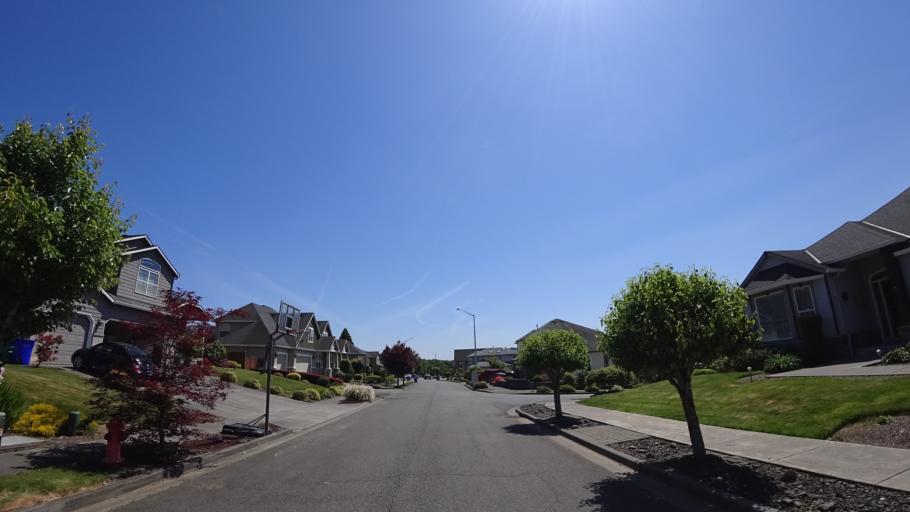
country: US
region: Oregon
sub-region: Clackamas County
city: Happy Valley
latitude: 45.4794
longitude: -122.4858
